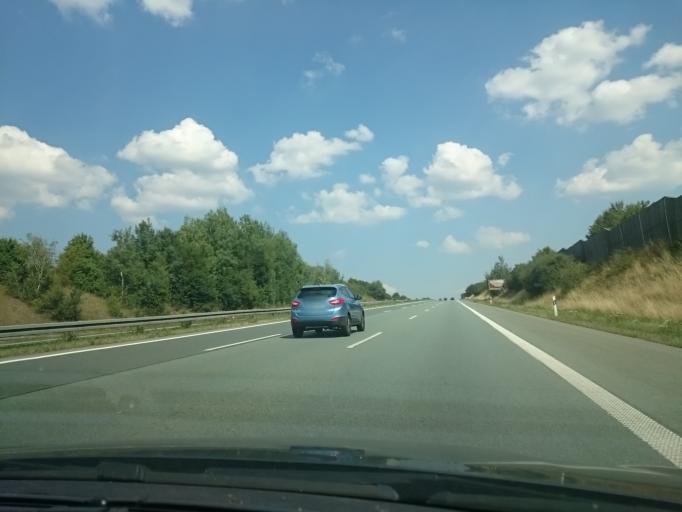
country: DE
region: Saxony
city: Neuensalz
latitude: 50.5251
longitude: 12.2390
